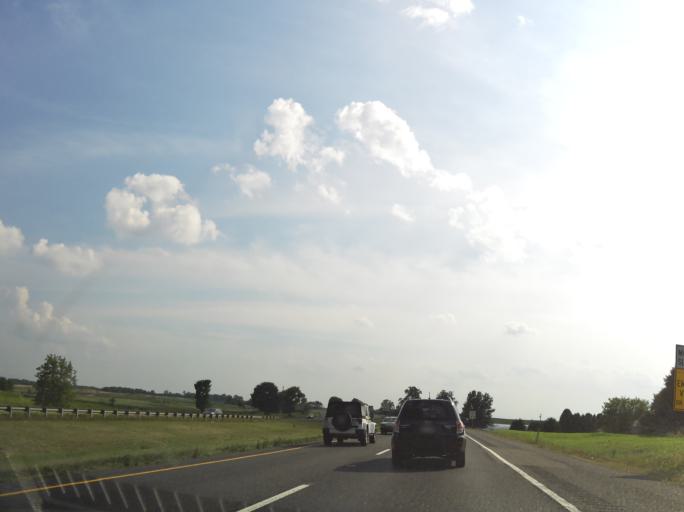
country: US
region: Pennsylvania
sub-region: Franklin County
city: State Line
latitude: 39.7163
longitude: -77.7391
